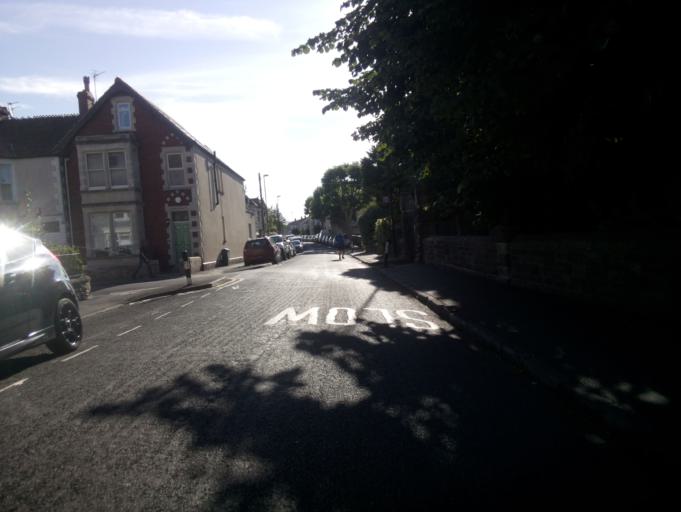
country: GB
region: England
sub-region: South Gloucestershire
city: Kingswood
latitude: 51.4582
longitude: -2.5443
